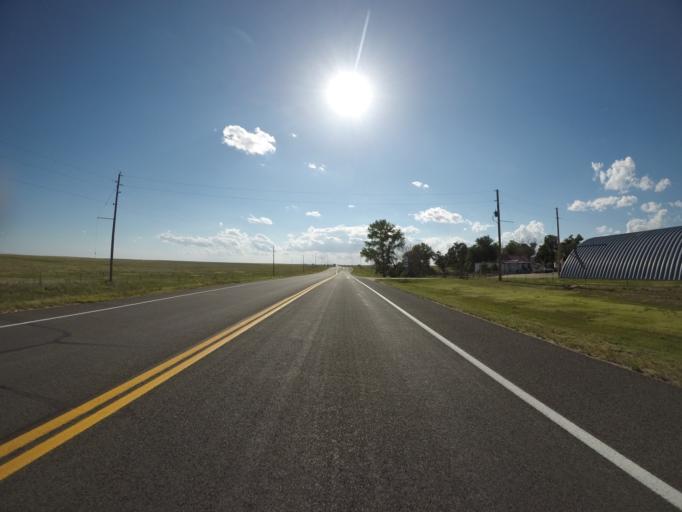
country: US
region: Colorado
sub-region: Morgan County
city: Fort Morgan
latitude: 40.6113
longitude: -103.7973
